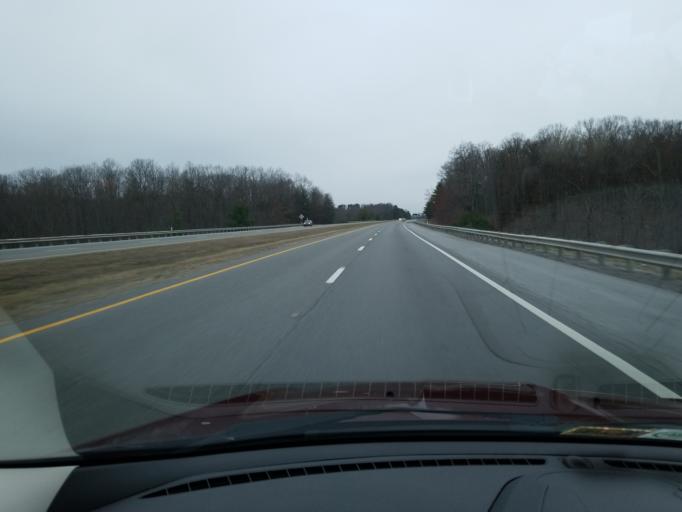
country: US
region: West Virginia
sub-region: Mercer County
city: Athens
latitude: 37.3562
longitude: -81.0218
